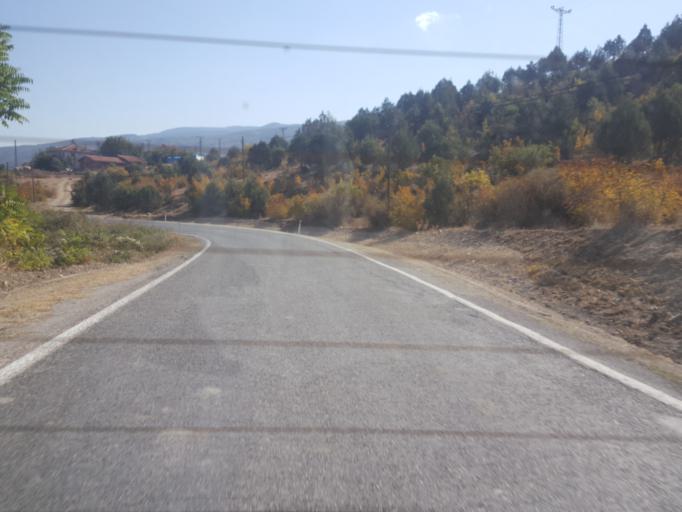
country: TR
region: Kastamonu
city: Tosya
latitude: 40.9950
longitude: 34.1372
